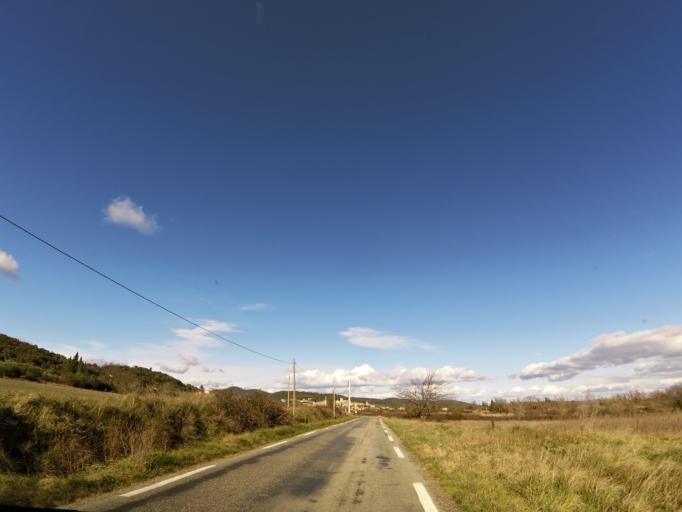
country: FR
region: Languedoc-Roussillon
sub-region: Departement du Gard
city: Sauve
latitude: 43.9815
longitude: 3.9497
